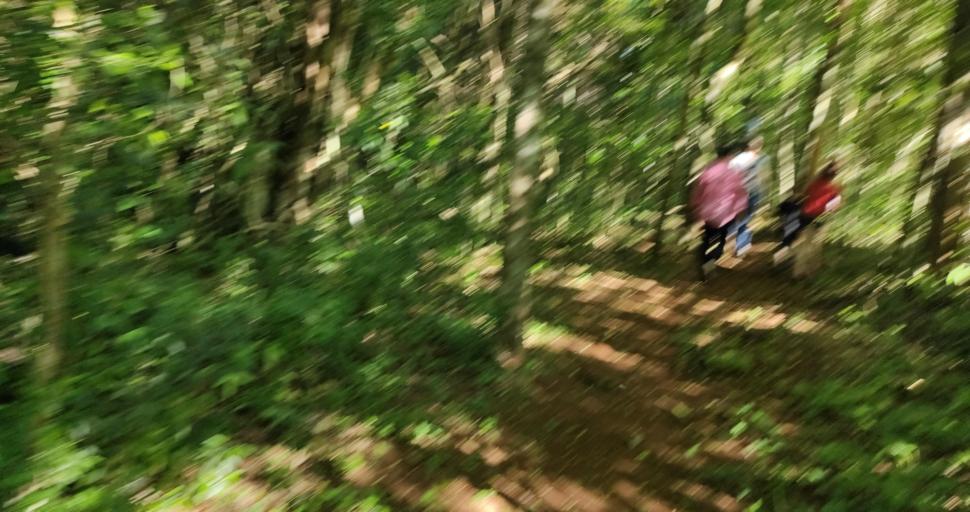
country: AR
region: Misiones
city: Capiovi
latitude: -26.9155
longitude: -55.0910
